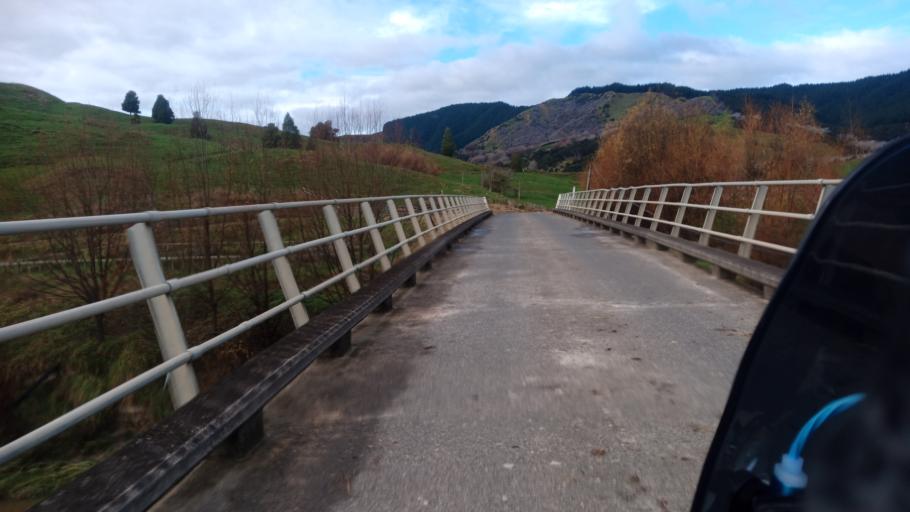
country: NZ
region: Gisborne
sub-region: Gisborne District
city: Gisborne
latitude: -38.4336
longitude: 177.8982
